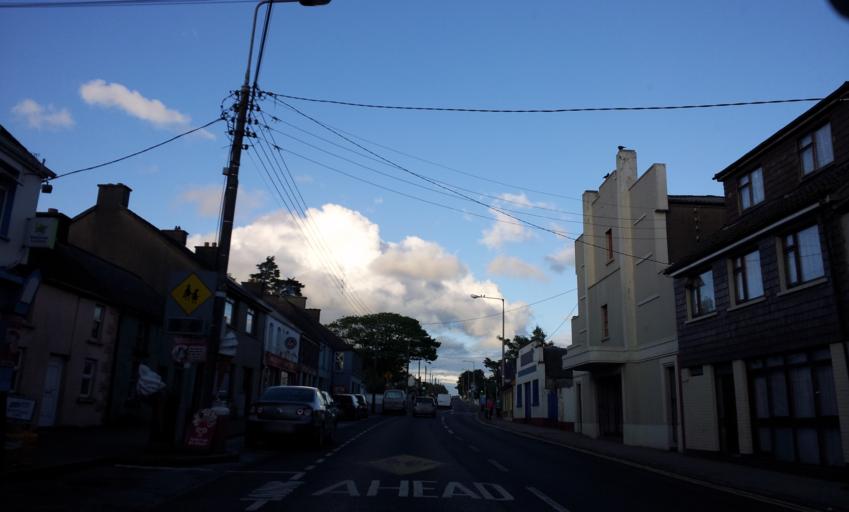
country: IE
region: Munster
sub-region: County Limerick
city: Abbeyfeale
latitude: 52.3860
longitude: -9.2976
